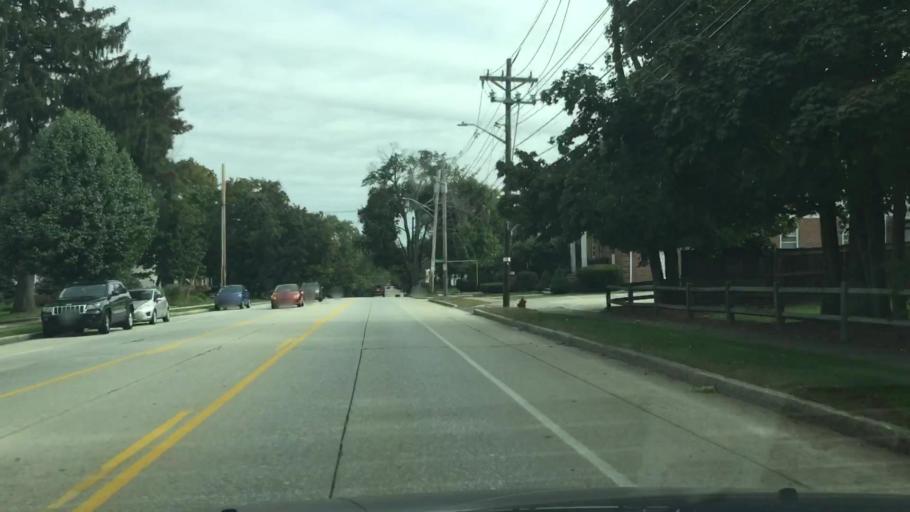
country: US
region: Massachusetts
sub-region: Middlesex County
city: Lowell
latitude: 42.6422
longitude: -71.2956
